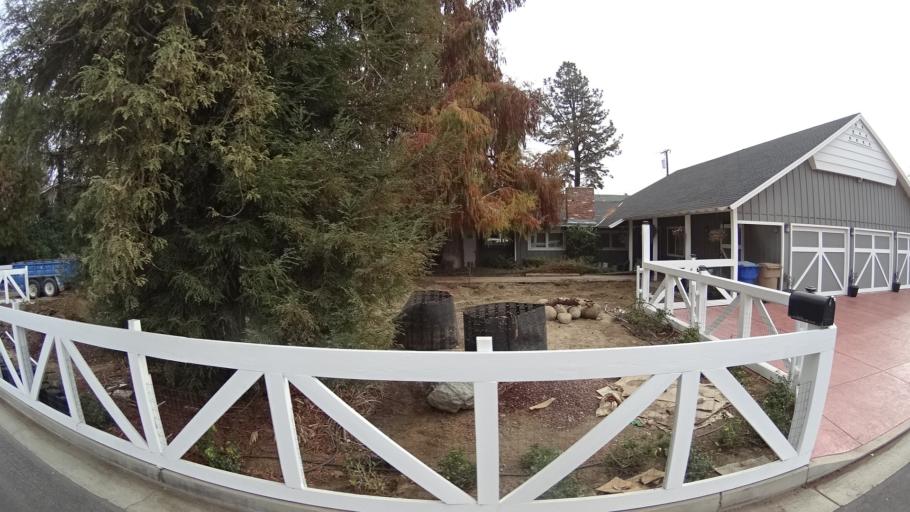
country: US
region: California
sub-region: Kern County
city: Bakersfield
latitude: 35.3566
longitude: -119.0378
